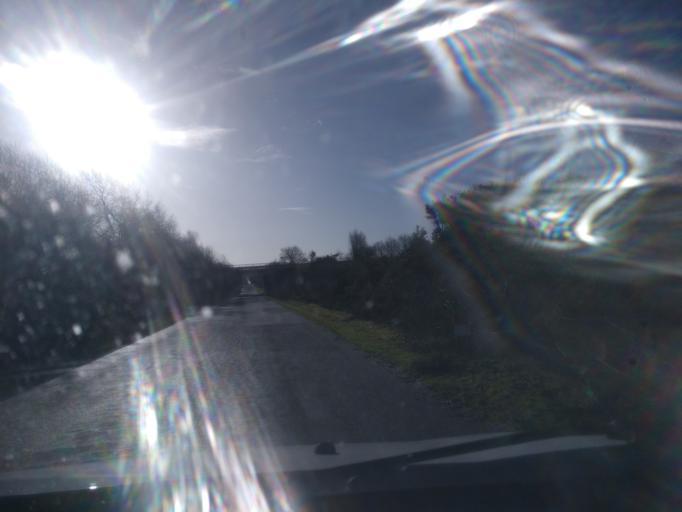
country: FR
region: Brittany
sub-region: Departement d'Ille-et-Vilaine
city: Saint-Broladre
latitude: 48.5648
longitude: -1.6411
